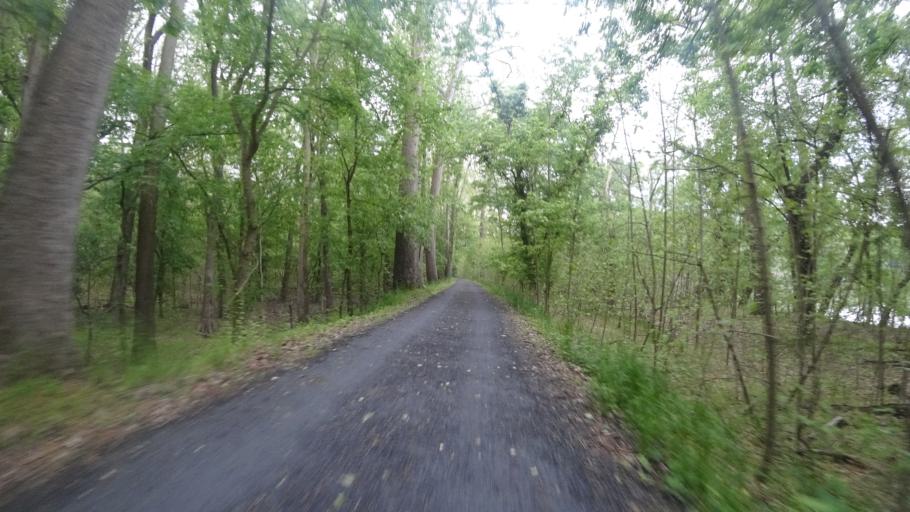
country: US
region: West Virginia
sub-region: Jefferson County
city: Bolivar
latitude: 39.3391
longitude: -77.7567
